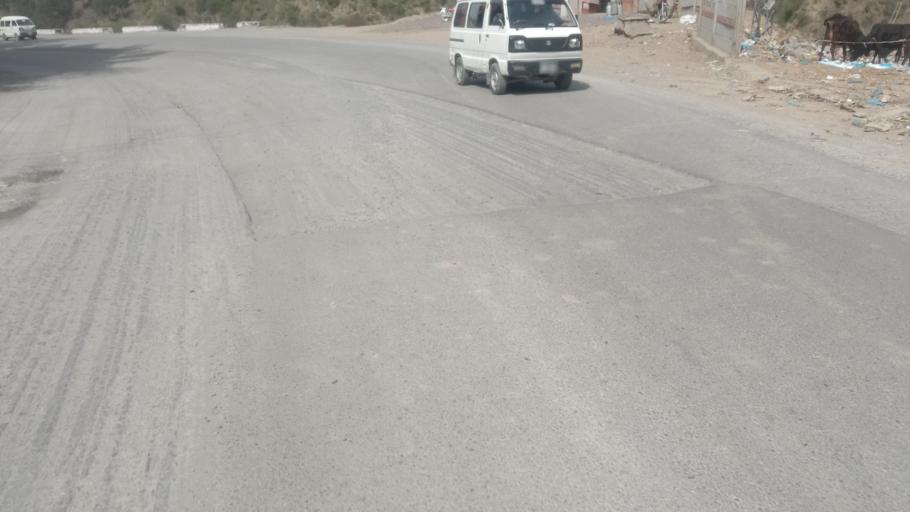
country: PK
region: Khyber Pakhtunkhwa
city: Abbottabad
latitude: 34.1238
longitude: 73.1888
